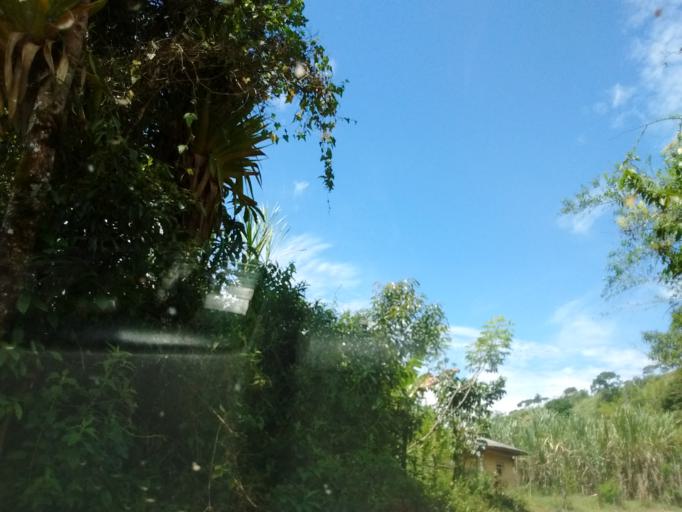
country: CO
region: Cauca
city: Villa Rica
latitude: 2.6599
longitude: -76.7673
